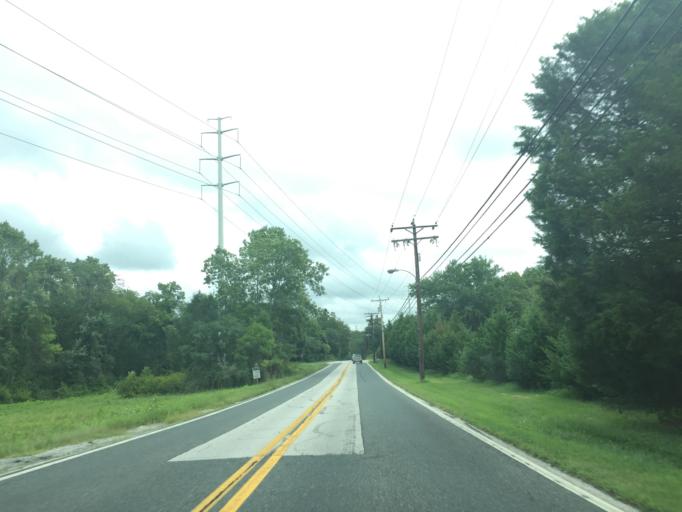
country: US
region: Maryland
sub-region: Baltimore County
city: Kingsville
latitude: 39.4226
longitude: -76.3826
